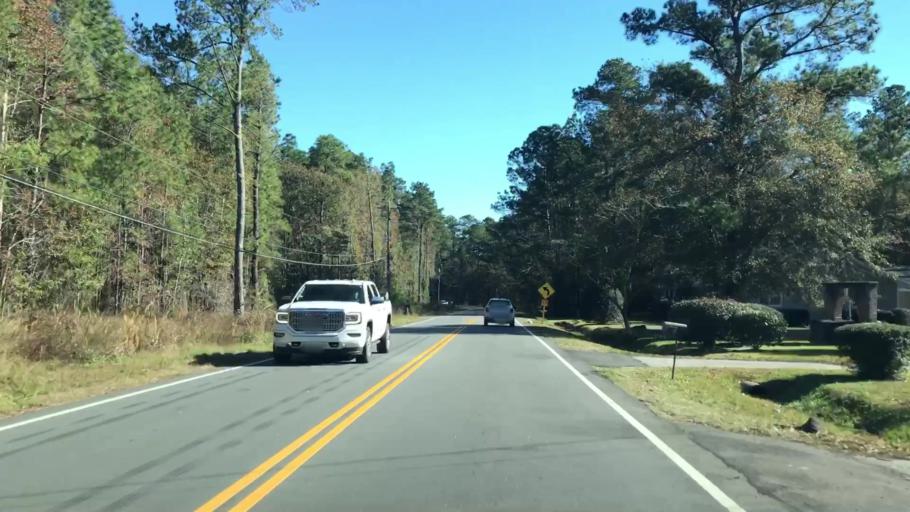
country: US
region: South Carolina
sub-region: Dorchester County
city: Summerville
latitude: 33.0231
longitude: -80.1988
